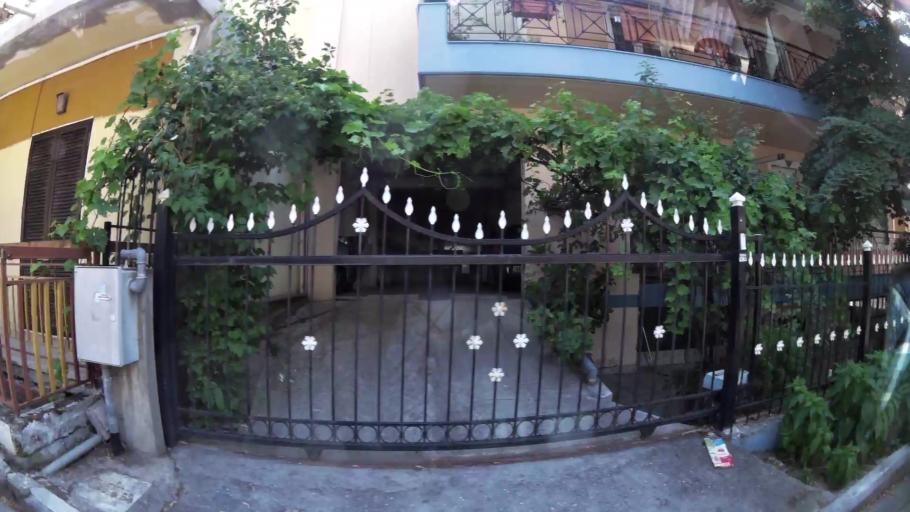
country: GR
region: Central Macedonia
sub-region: Nomos Thessalonikis
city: Evosmos
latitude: 40.6747
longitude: 22.9120
